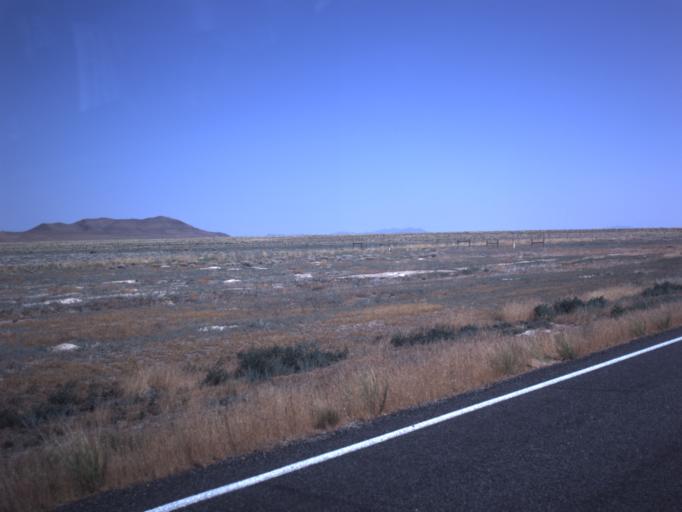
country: US
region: Utah
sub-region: Millard County
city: Delta
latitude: 39.0056
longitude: -112.7853
